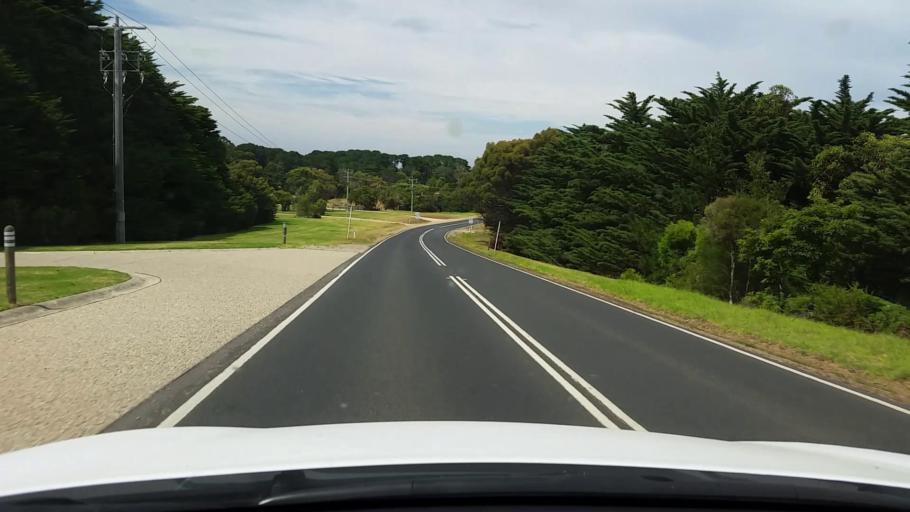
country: AU
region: Victoria
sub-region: Mornington Peninsula
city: Merricks
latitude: -38.4605
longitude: 145.0209
